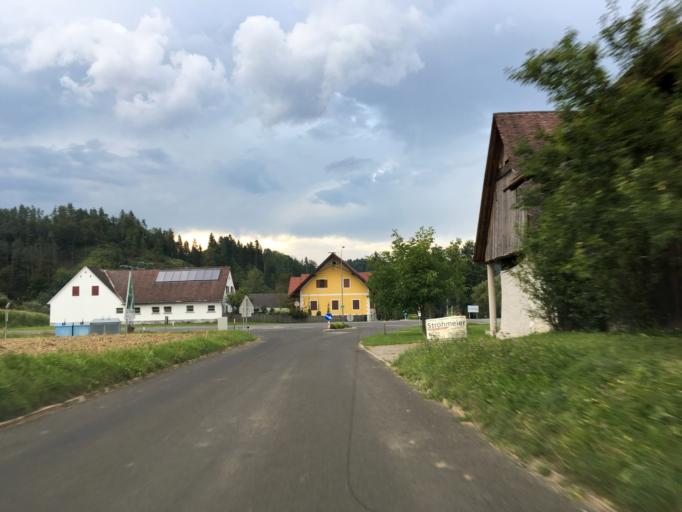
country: AT
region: Styria
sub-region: Politischer Bezirk Leibnitz
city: Oberhaag
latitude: 46.6848
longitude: 15.3522
